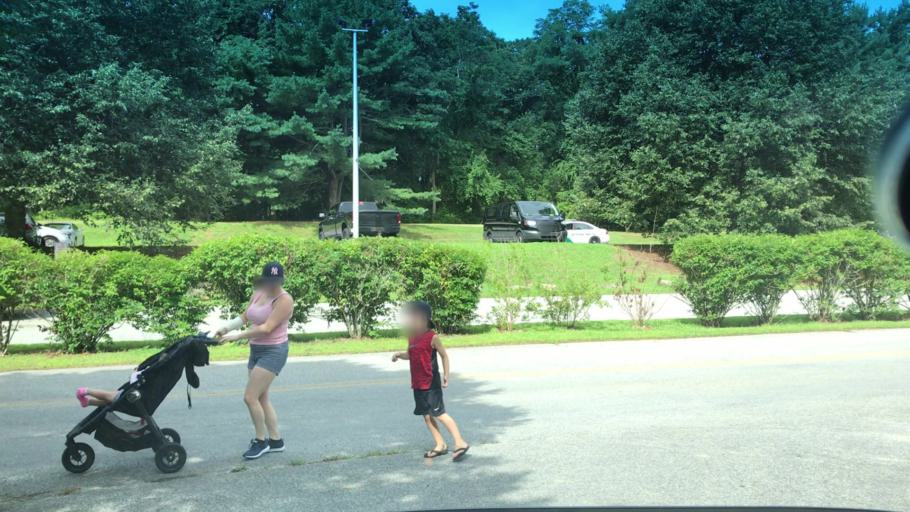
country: US
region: New York
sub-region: Suffolk County
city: Wading River
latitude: 40.9616
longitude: -72.8042
